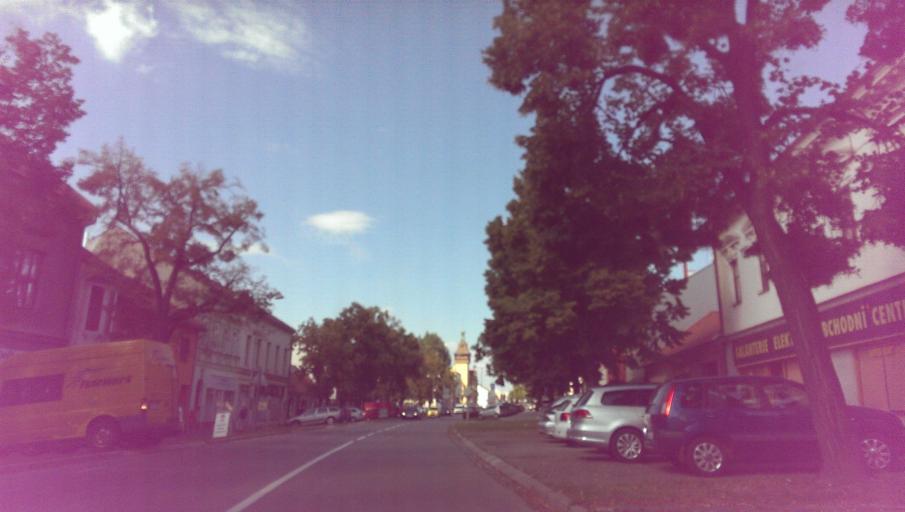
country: CZ
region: Zlin
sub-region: Okres Zlin
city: Napajedla
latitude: 49.1710
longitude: 17.5119
